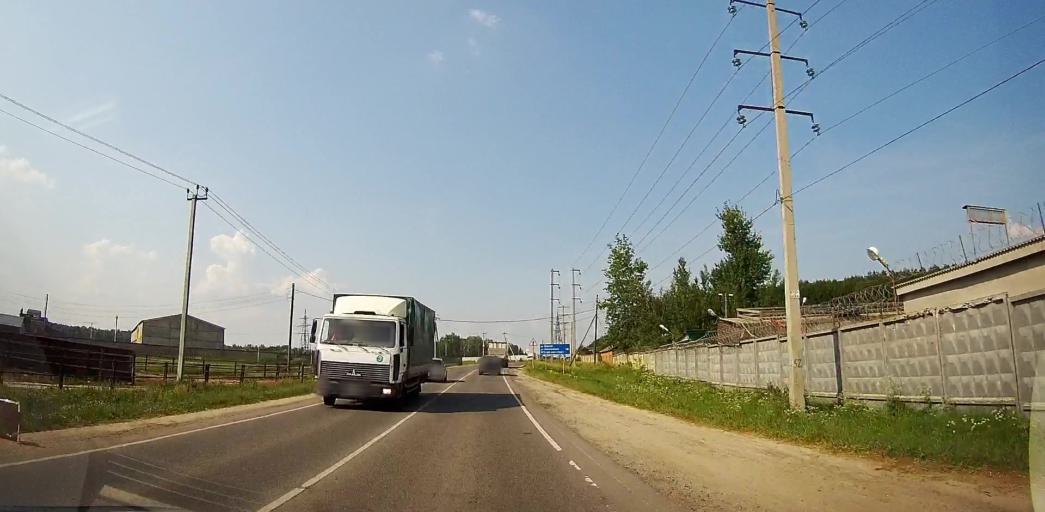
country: RU
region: Moskovskaya
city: Barybino
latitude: 55.2776
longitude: 37.9159
